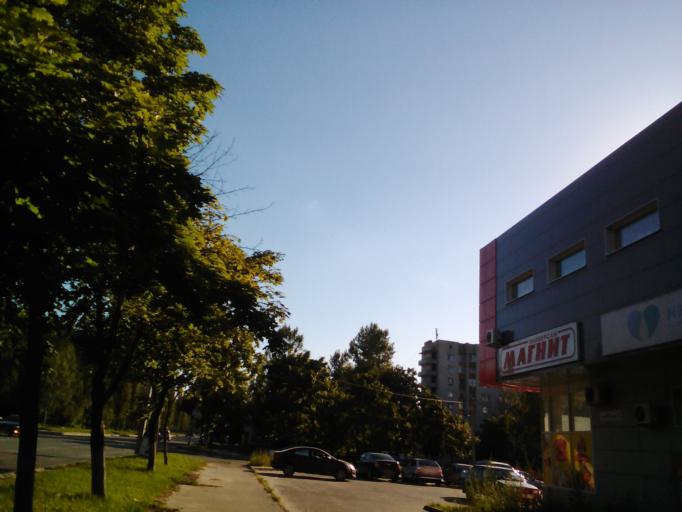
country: RU
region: Kursk
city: Voroshnevo
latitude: 51.6664
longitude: 36.0729
